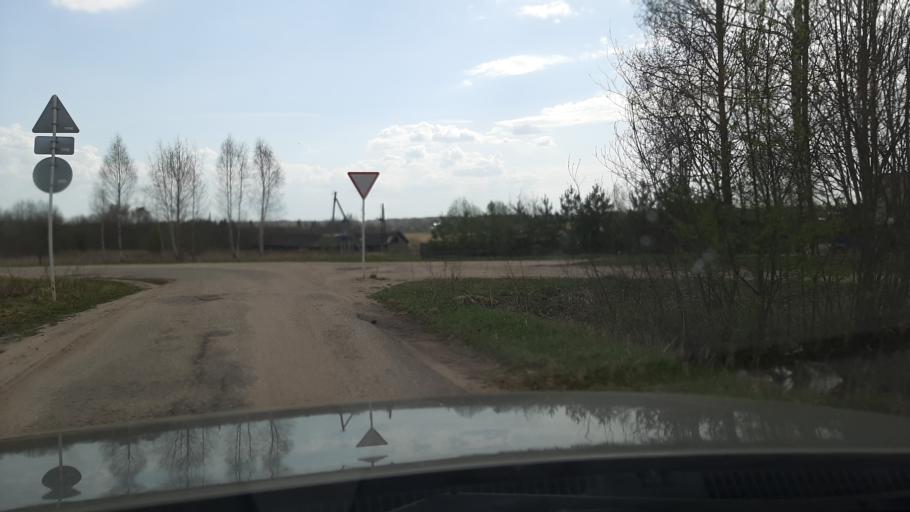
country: RU
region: Ivanovo
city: Furmanov
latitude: 57.2996
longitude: 41.1664
